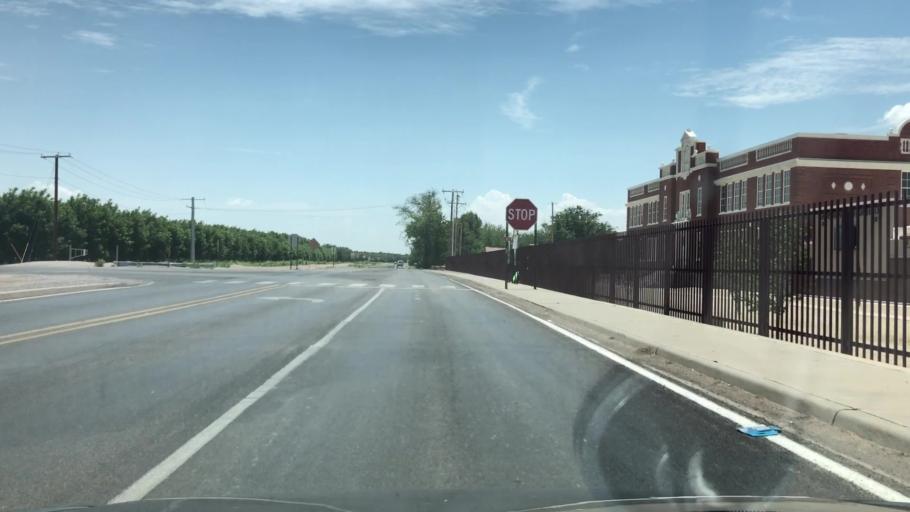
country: US
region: New Mexico
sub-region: Dona Ana County
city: La Union
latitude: 31.9980
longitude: -106.6558
